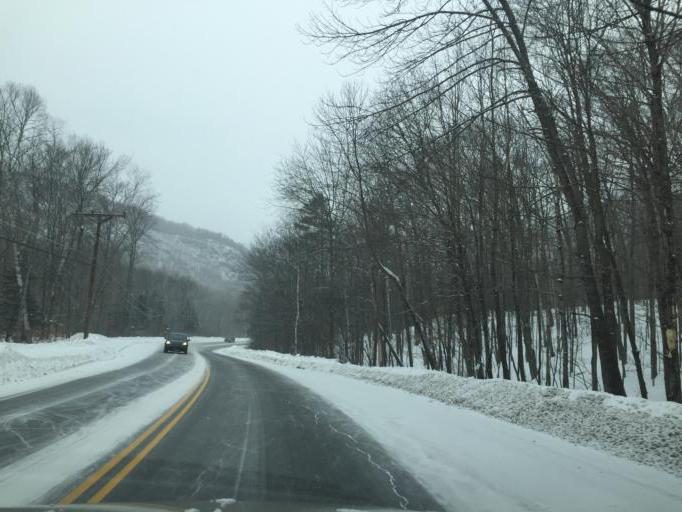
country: US
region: New Hampshire
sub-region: Carroll County
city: North Conway
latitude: 44.1791
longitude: -71.2255
